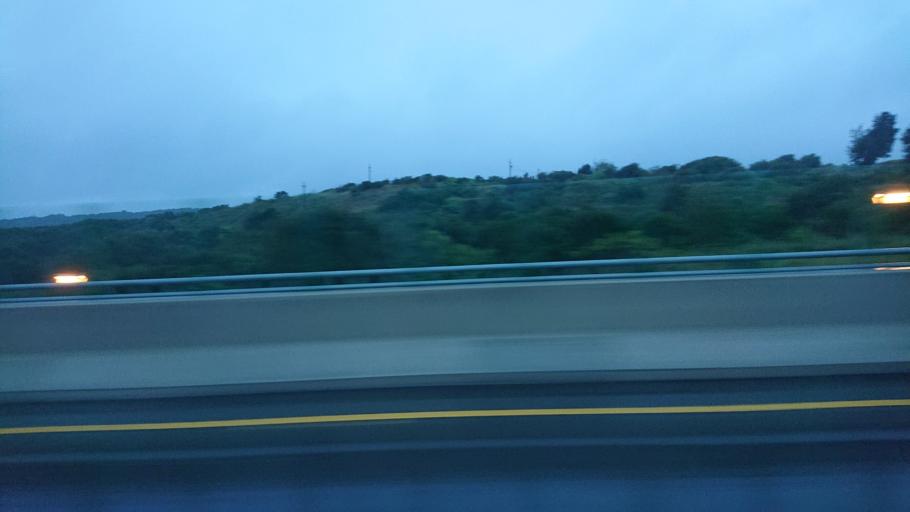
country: TW
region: Taiwan
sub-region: Miaoli
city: Miaoli
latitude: 24.5696
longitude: 120.7154
